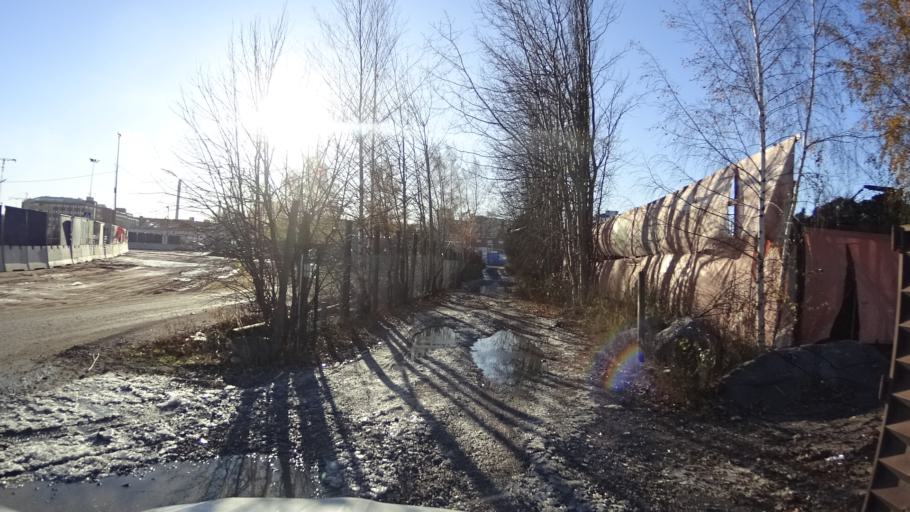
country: FI
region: Uusimaa
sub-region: Helsinki
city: Helsinki
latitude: 60.1958
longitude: 24.9784
